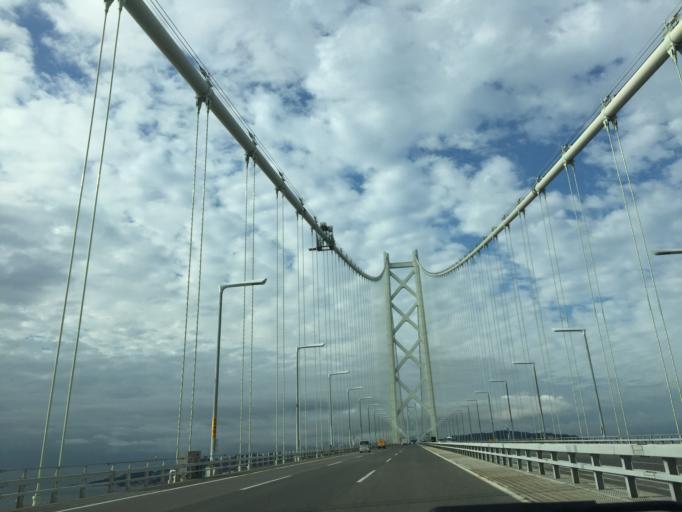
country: JP
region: Hyogo
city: Akashi
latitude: 34.6292
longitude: 135.0317
